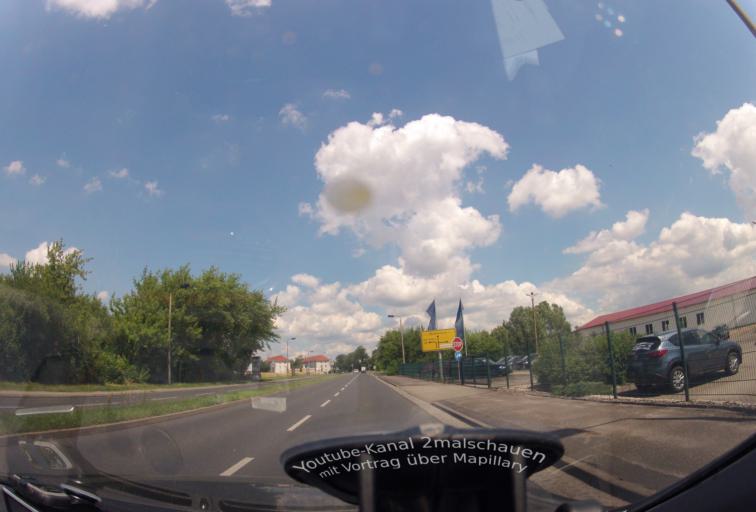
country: DE
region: Saxony
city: Zinna
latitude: 51.5629
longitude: 12.9742
